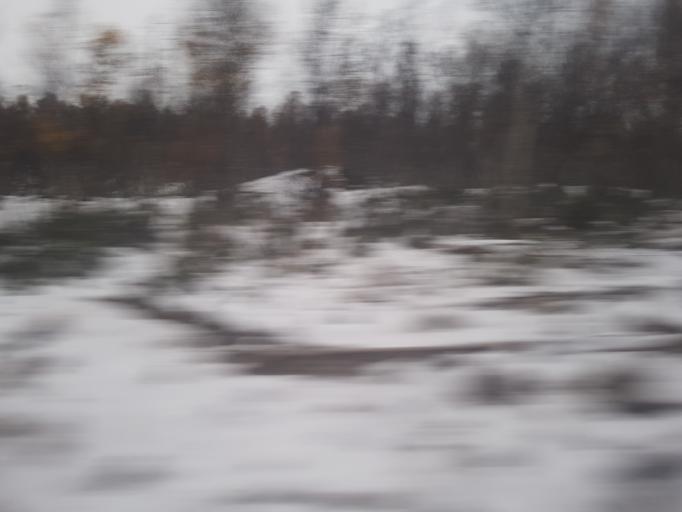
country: NO
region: Oppland
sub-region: Dovre
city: Dovre
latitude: 62.1772
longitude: 9.4525
